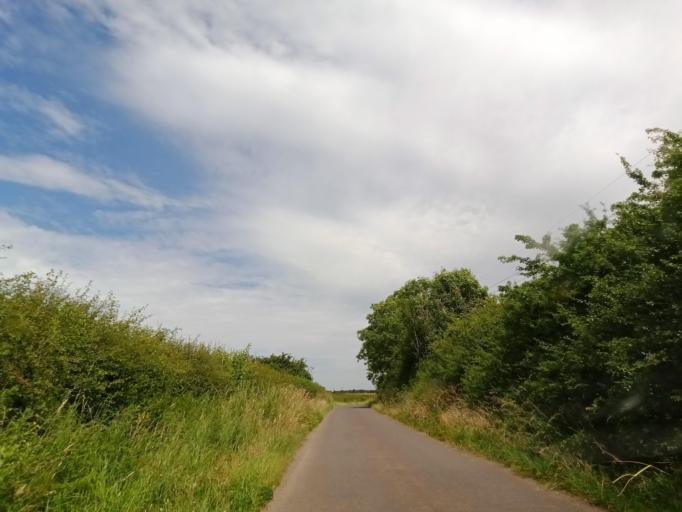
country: IE
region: Leinster
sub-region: Kilkenny
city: Thomastown
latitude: 52.5741
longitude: -7.1263
